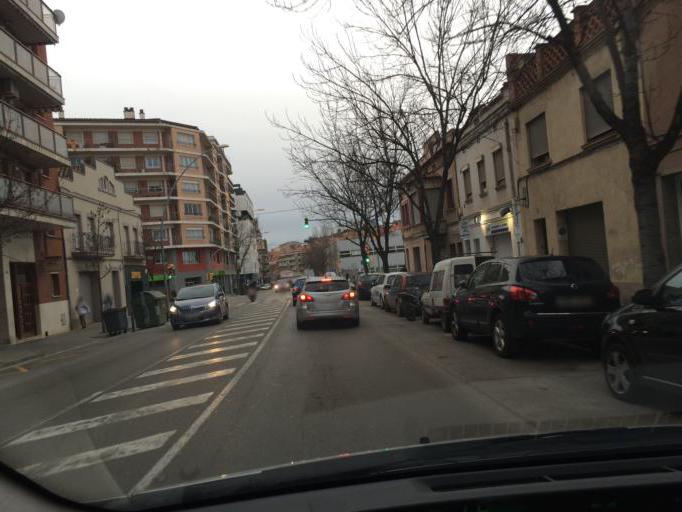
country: ES
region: Catalonia
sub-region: Provincia de Barcelona
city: Manresa
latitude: 41.7360
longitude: 1.8260
